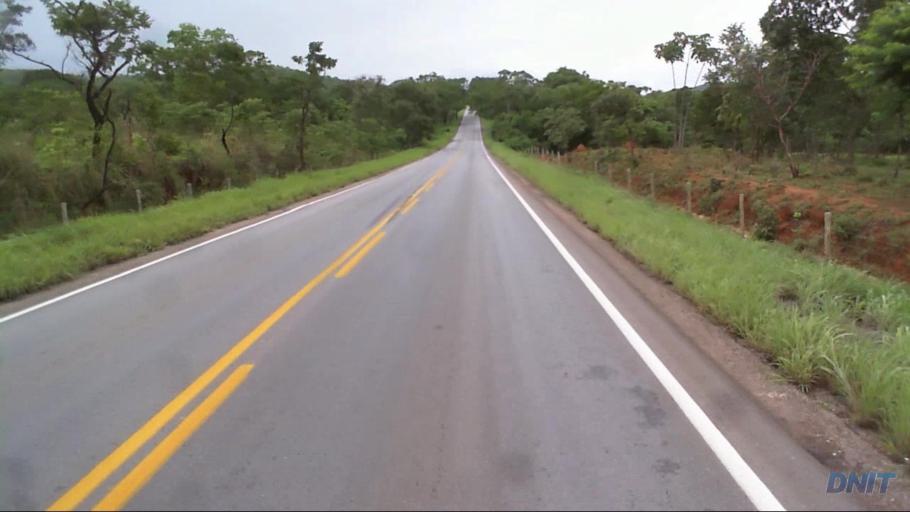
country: BR
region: Goias
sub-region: Padre Bernardo
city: Padre Bernardo
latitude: -15.4468
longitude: -48.2037
